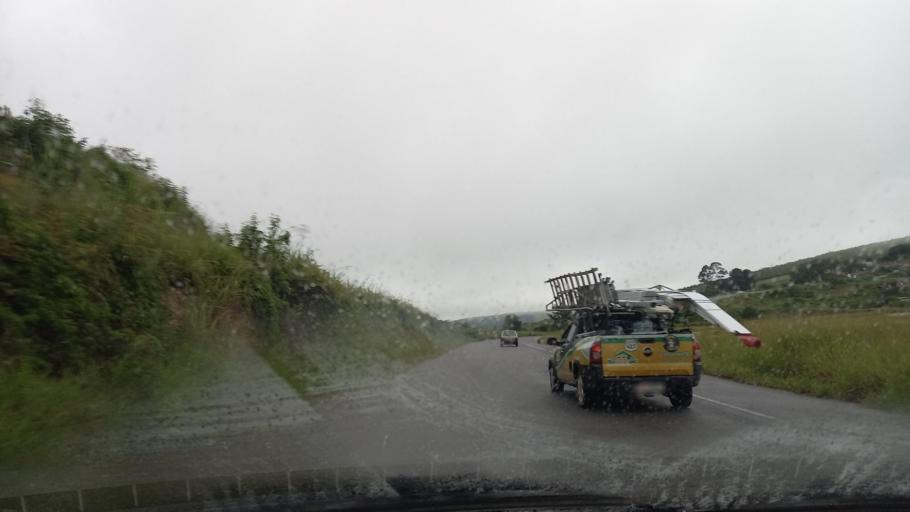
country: BR
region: Pernambuco
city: Garanhuns
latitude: -8.8772
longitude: -36.5054
